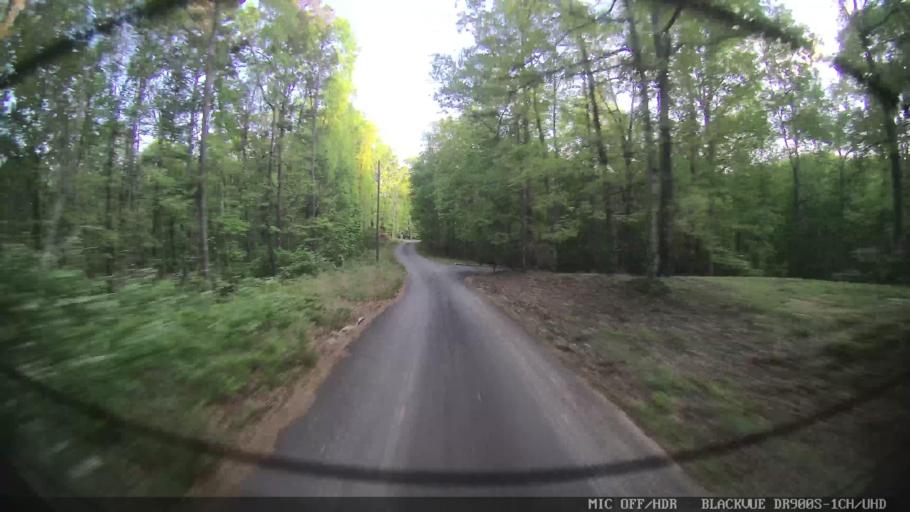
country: US
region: Georgia
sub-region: Bartow County
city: Emerson
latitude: 34.0839
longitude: -84.7719
